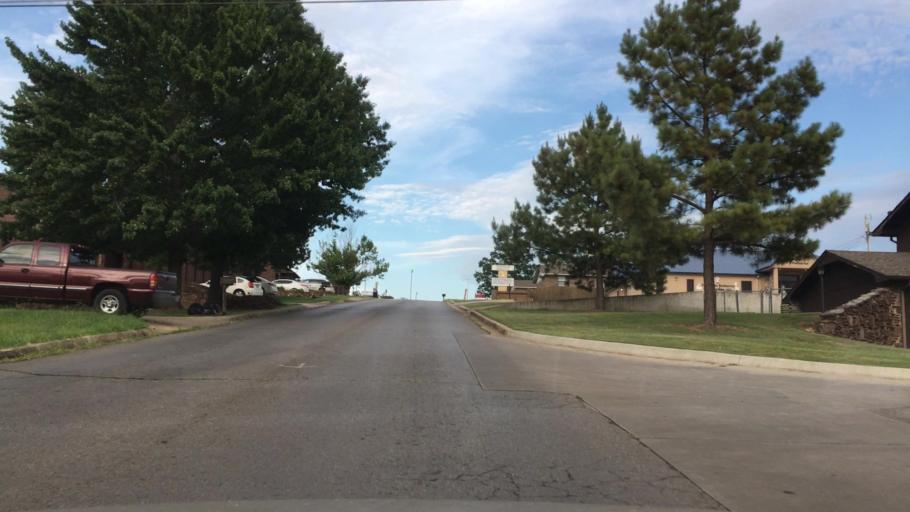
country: US
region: Oklahoma
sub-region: Cherokee County
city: Tahlequah
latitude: 35.9126
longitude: -94.9529
